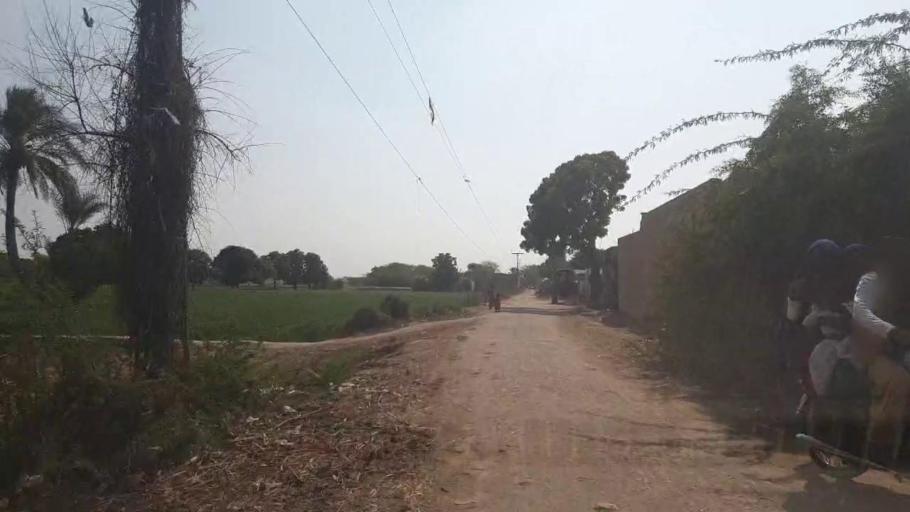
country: PK
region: Sindh
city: Mirpur Khas
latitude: 25.4903
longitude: 68.8820
